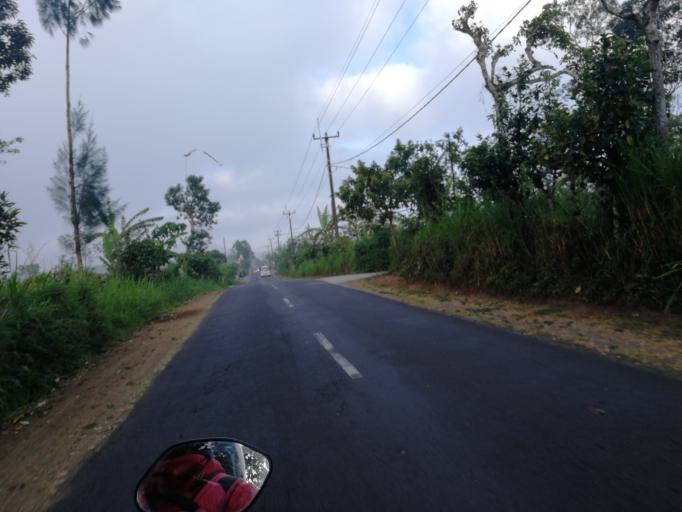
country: ID
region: Bali
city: Banjar Kedisan
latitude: -8.2239
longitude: 115.2535
